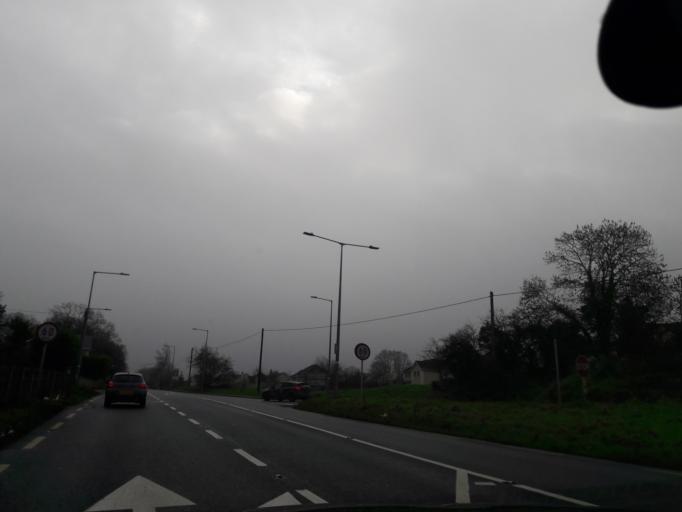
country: IE
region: Ulster
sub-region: County Donegal
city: Leifear
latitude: 54.8414
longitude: -7.4969
